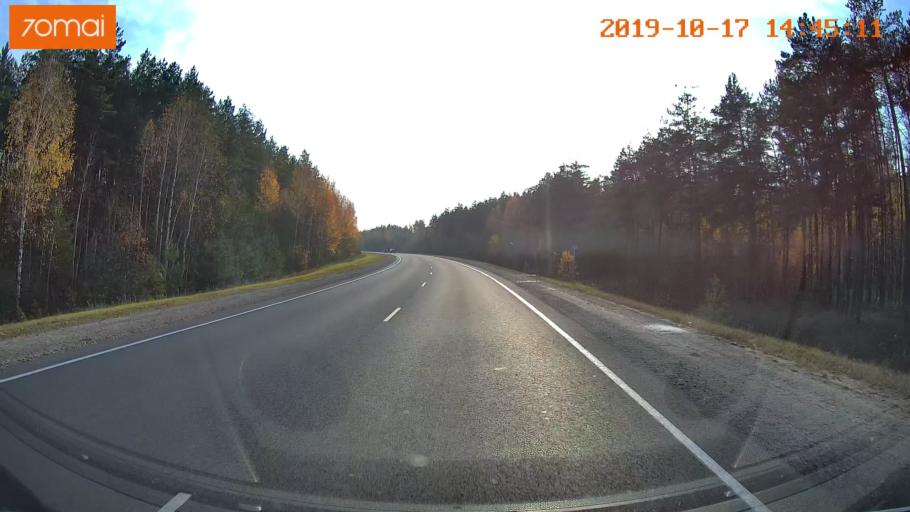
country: RU
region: Rjazan
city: Solotcha
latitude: 54.8034
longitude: 39.8792
